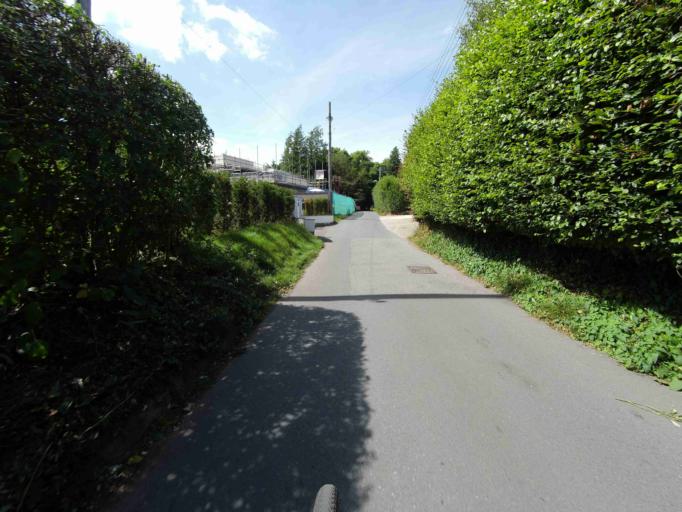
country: GB
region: England
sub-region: Devon
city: Topsham
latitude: 50.6719
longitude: -3.4439
